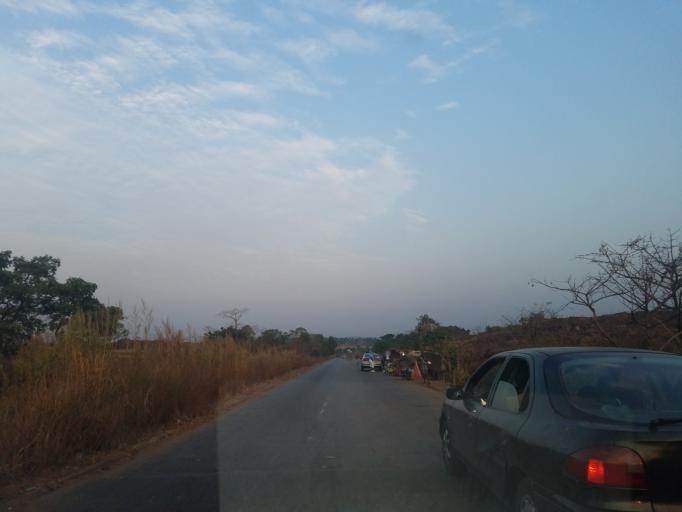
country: GN
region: Boke
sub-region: Fria
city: Fria
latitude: 10.0880
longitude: -13.6717
